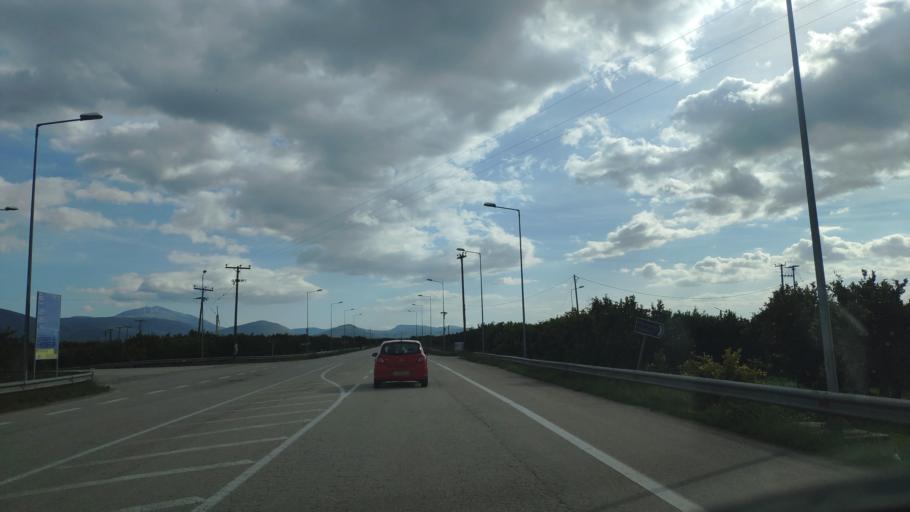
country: GR
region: Peloponnese
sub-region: Nomos Argolidos
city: Ayia Trias
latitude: 37.6784
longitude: 22.7716
